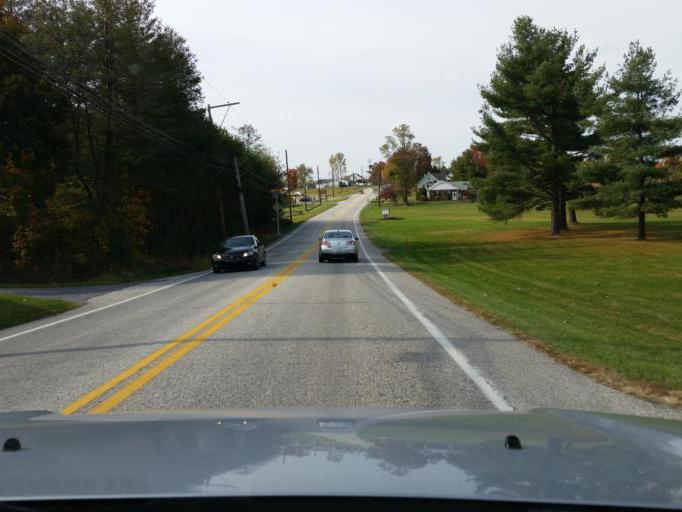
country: US
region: Pennsylvania
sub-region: Dauphin County
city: Skyline View
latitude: 40.3213
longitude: -76.7056
